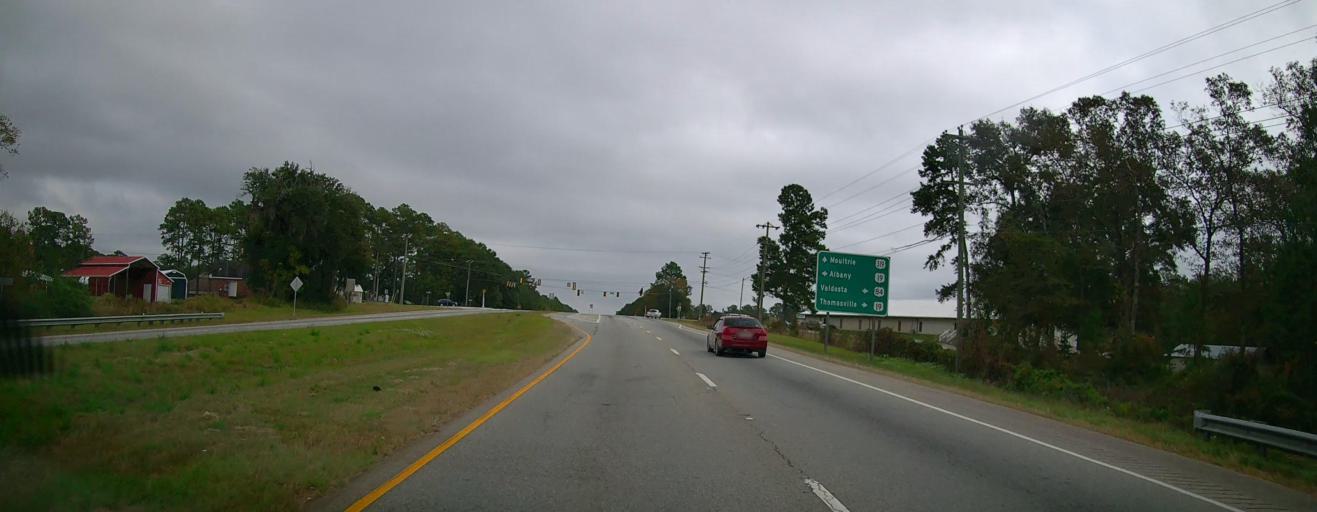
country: US
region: Georgia
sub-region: Thomas County
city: Thomasville
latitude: 30.8741
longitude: -83.9588
